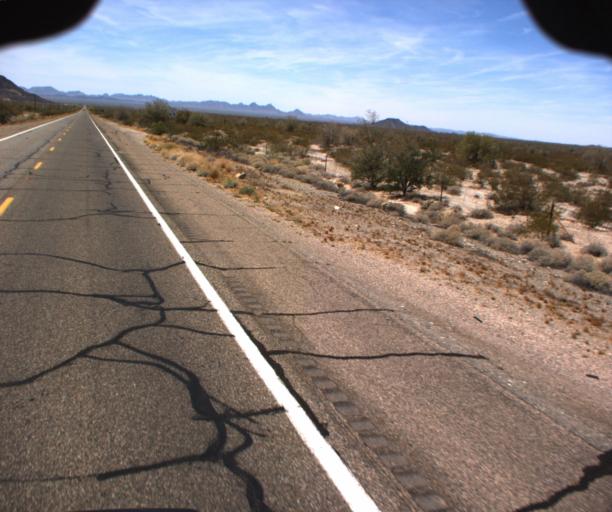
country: US
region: Arizona
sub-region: La Paz County
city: Salome
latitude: 33.7230
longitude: -113.7086
